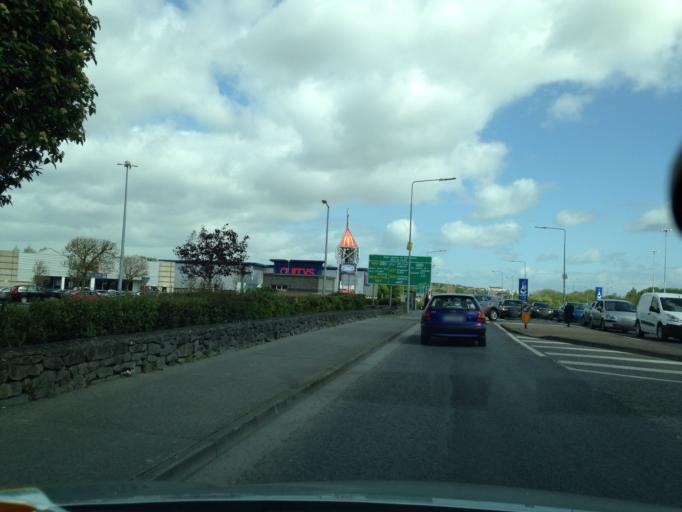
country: IE
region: Connaught
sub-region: County Galway
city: Gaillimh
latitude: 53.2798
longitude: -9.0496
